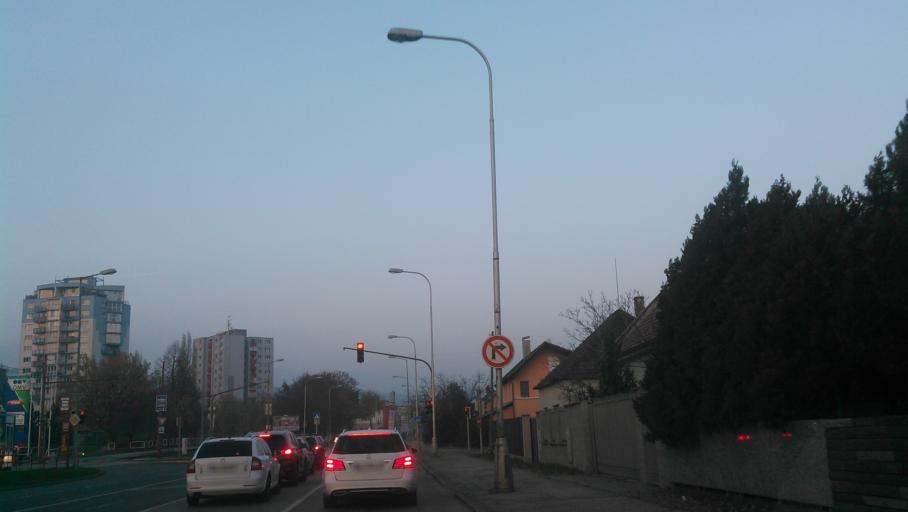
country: SK
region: Bratislavsky
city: Bratislava
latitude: 48.2025
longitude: 17.1494
